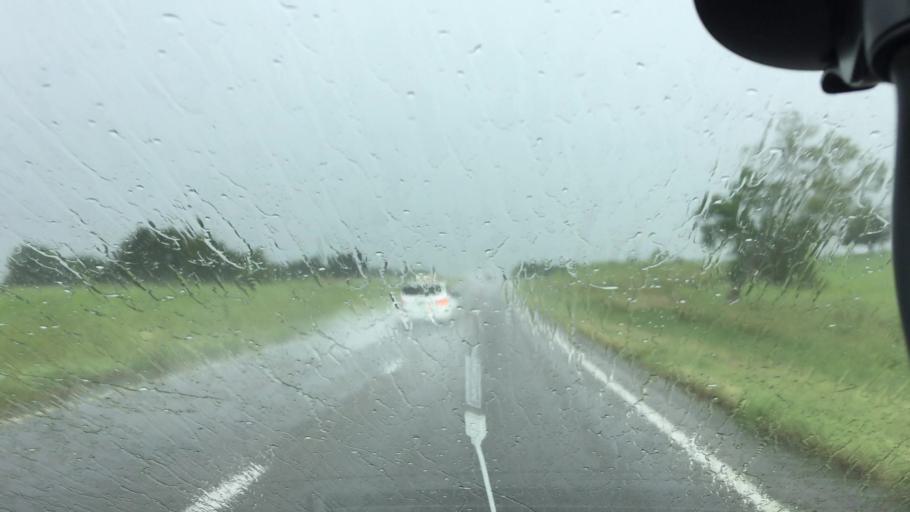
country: US
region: Alabama
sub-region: Montgomery County
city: Pike Road
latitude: 32.2209
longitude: -86.1180
